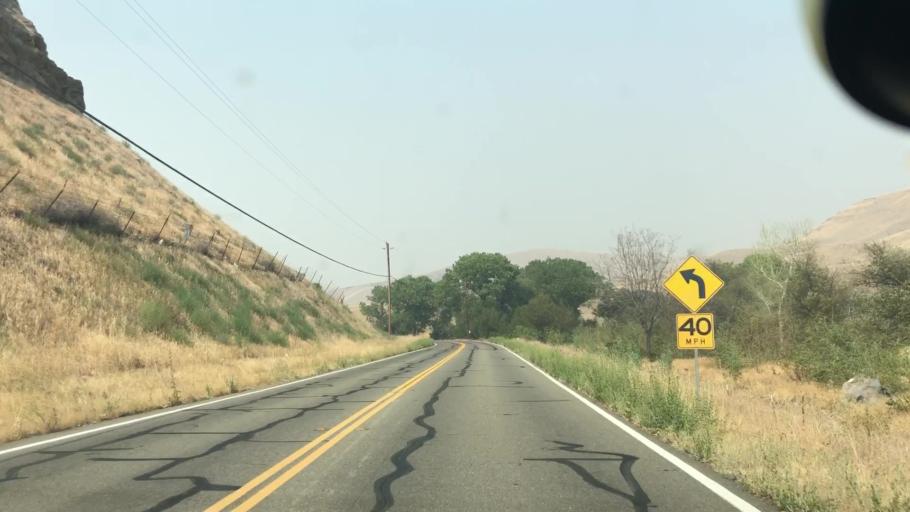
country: US
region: California
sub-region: San Joaquin County
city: Tracy
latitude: 37.6382
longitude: -121.4924
